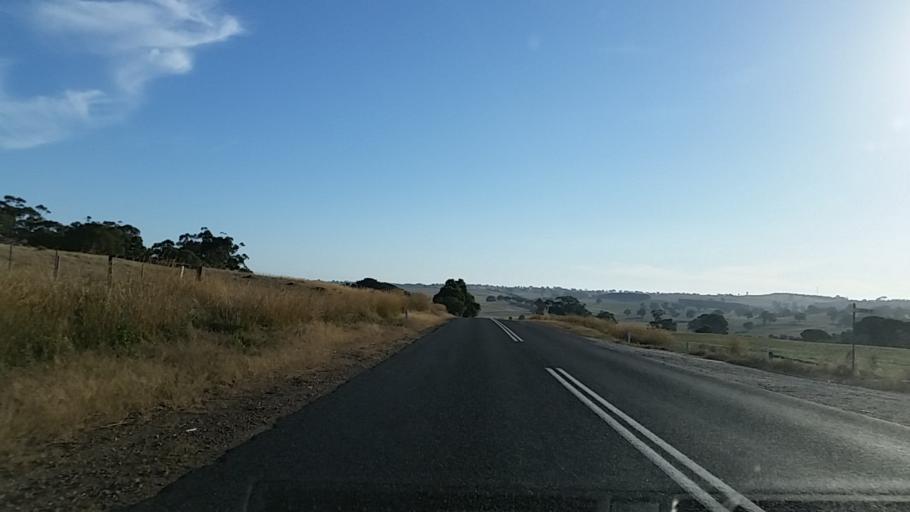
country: AU
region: South Australia
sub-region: Adelaide Hills
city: Birdwood
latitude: -34.7740
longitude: 139.1009
